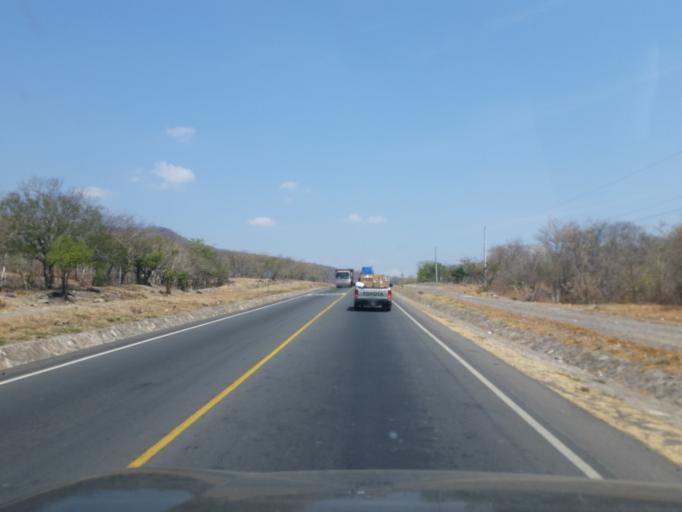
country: NI
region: Matagalpa
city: Ciudad Dario
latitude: 12.6044
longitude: -86.0457
